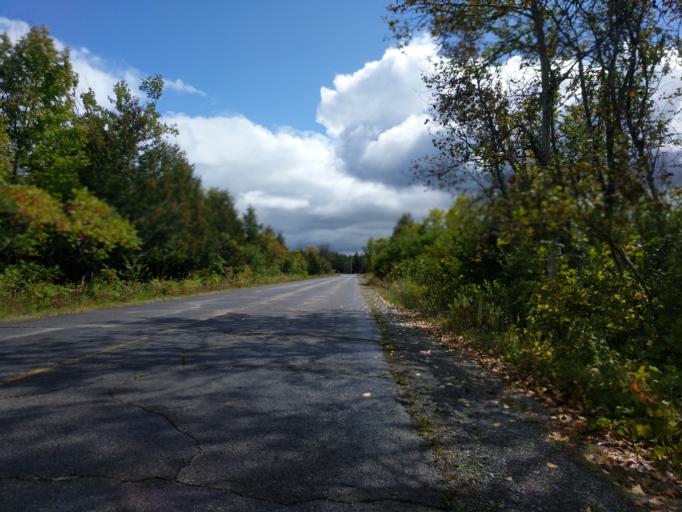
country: CA
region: Ontario
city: Bells Corners
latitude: 45.3137
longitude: -75.8619
